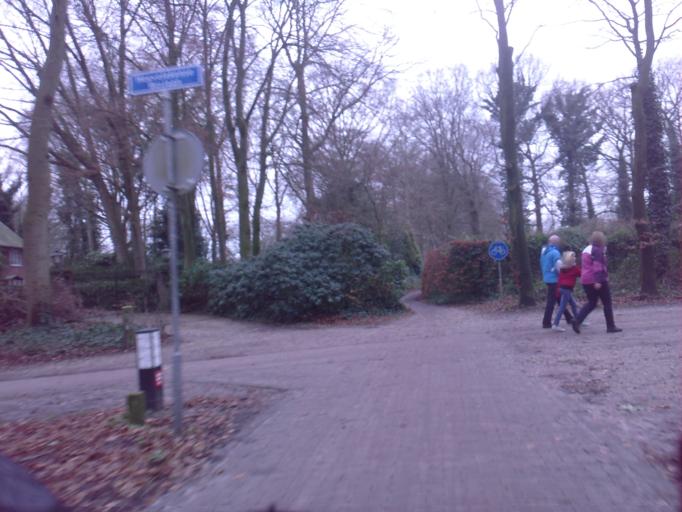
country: NL
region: Utrecht
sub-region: Gemeente Leusden
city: Leusden
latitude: 52.1837
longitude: 5.4436
